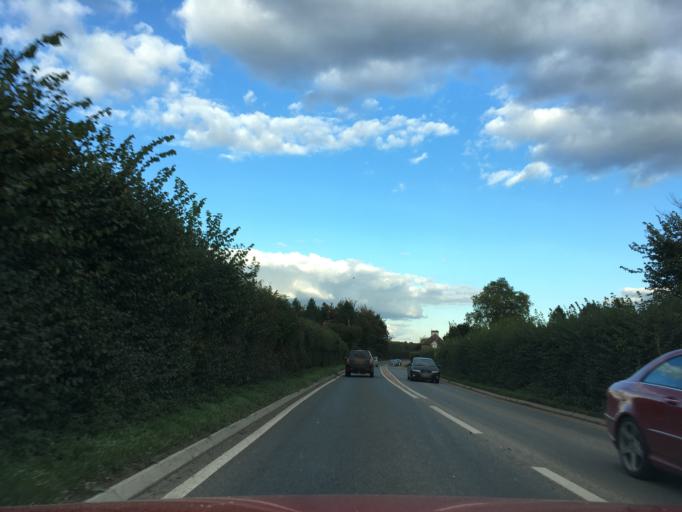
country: GB
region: England
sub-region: Herefordshire
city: Ocle Pychard
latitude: 52.0651
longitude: -2.5837
